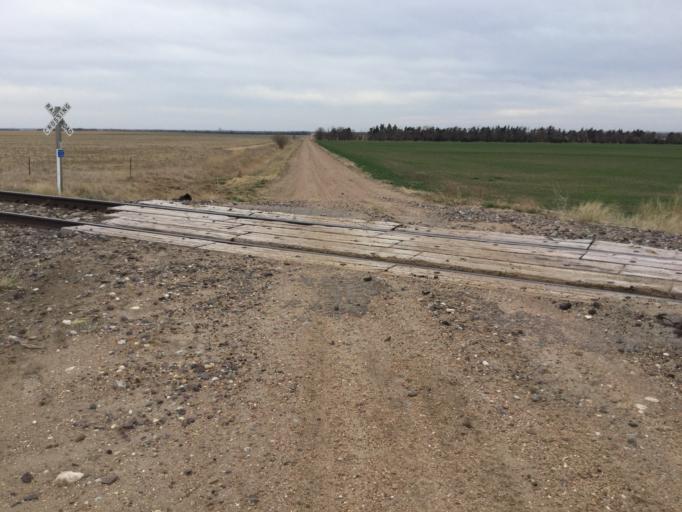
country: US
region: Kansas
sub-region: Barton County
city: Hoisington
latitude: 38.4971
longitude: -98.8855
